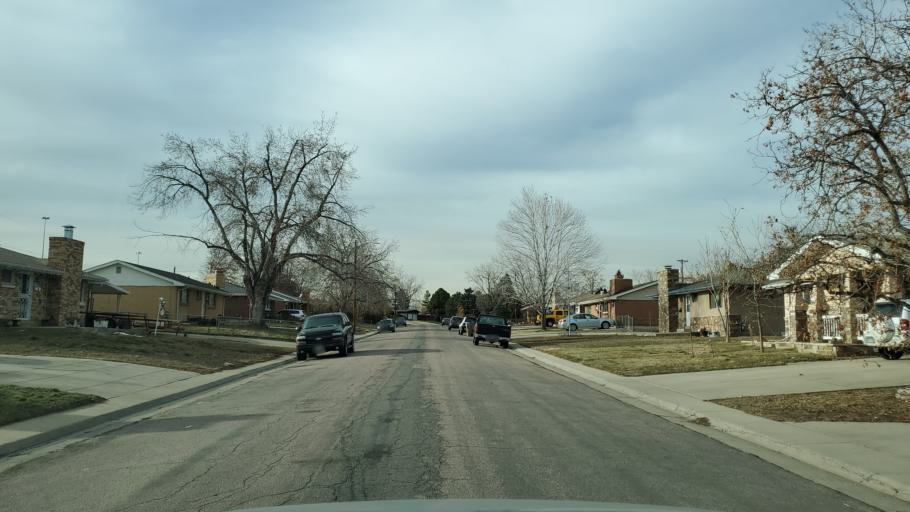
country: US
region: Colorado
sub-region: Adams County
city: Twin Lakes
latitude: 39.8351
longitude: -105.0185
